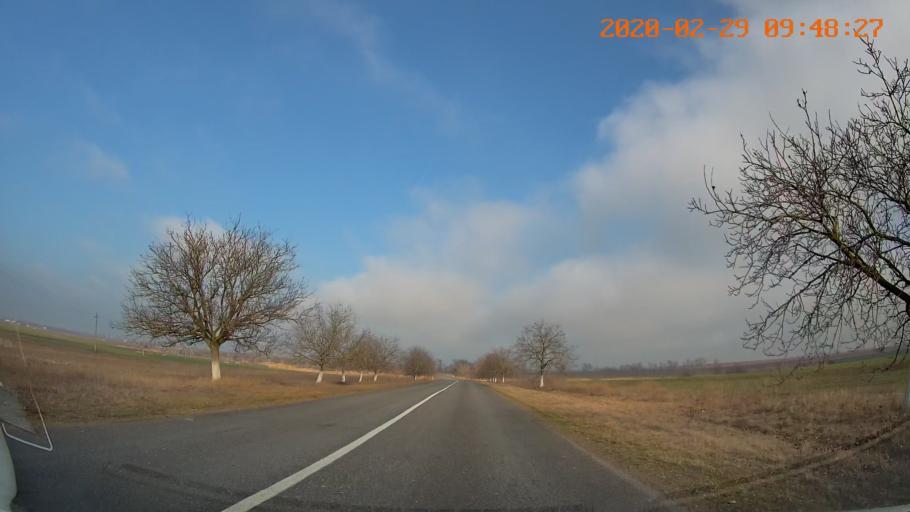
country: MD
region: Telenesti
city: Crasnoe
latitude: 46.6887
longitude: 29.7846
